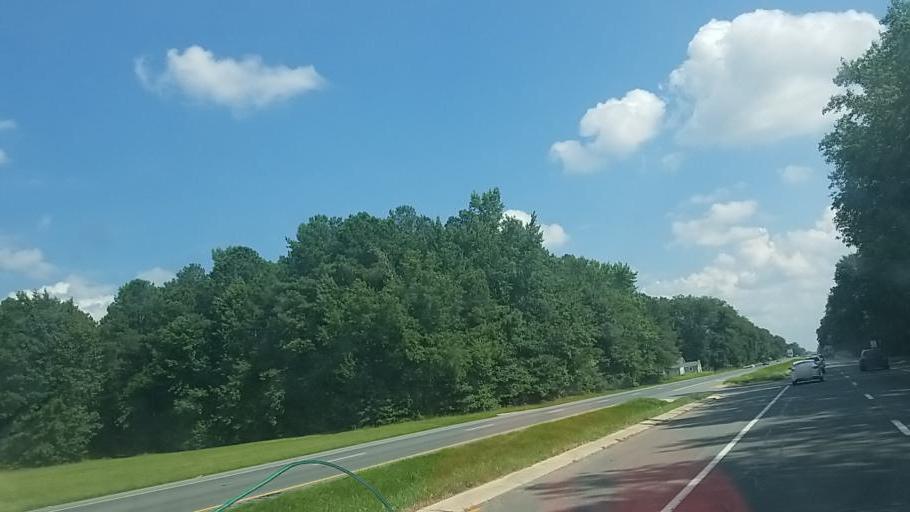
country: US
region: Delaware
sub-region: Sussex County
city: Georgetown
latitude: 38.6502
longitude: -75.3655
